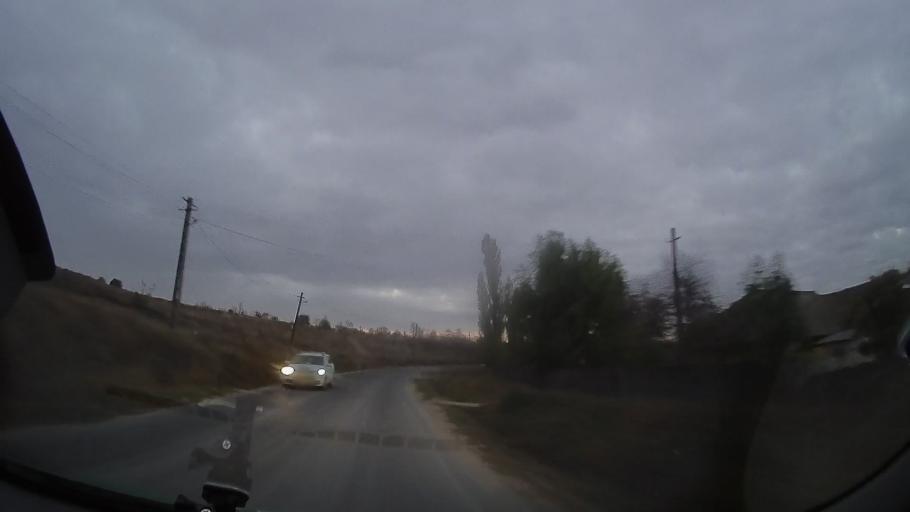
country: RO
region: Tulcea
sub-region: Comuna Mihai Bravu
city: Turda
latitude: 44.9686
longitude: 28.6291
